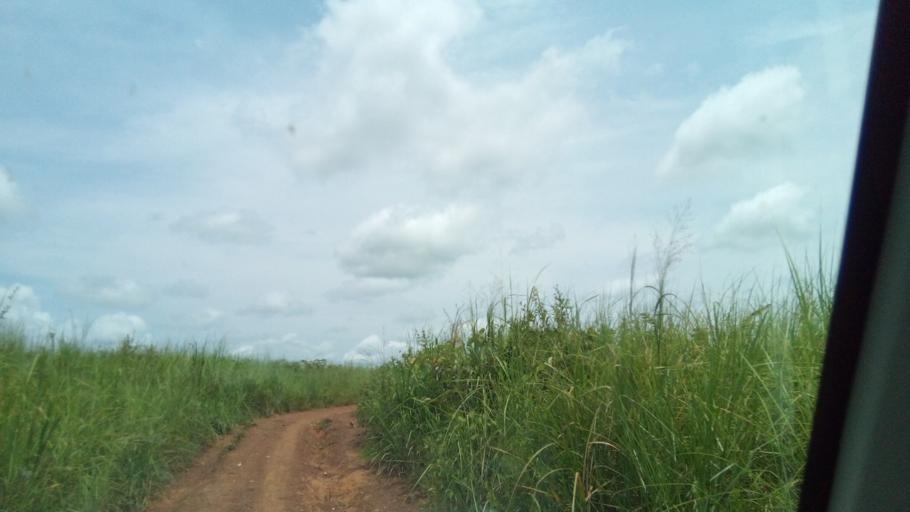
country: AO
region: Zaire
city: Mbanza Congo
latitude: -5.7932
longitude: 13.9933
